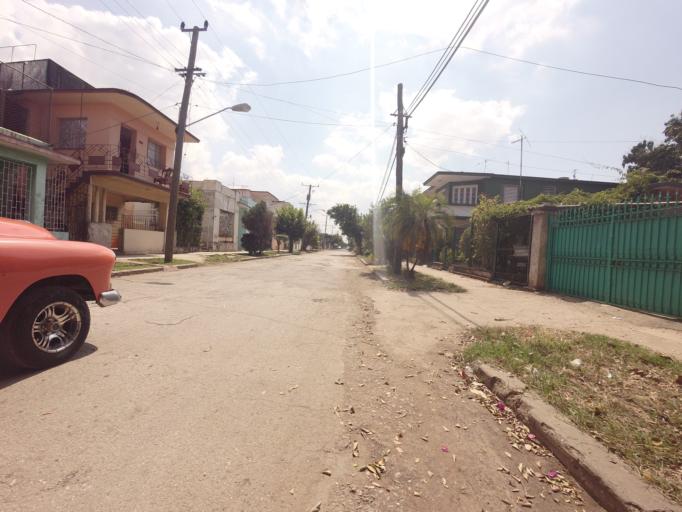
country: CU
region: La Habana
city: Cerro
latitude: 23.1034
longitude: -82.4303
